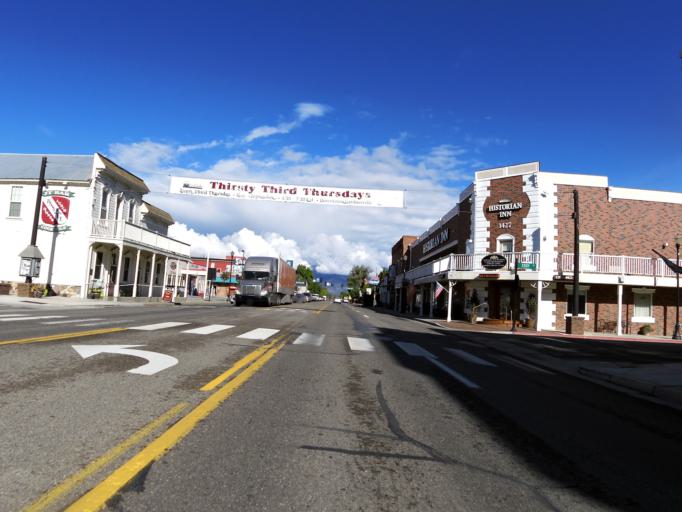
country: US
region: Nevada
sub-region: Douglas County
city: Gardnerville
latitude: 38.9406
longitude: -119.7483
